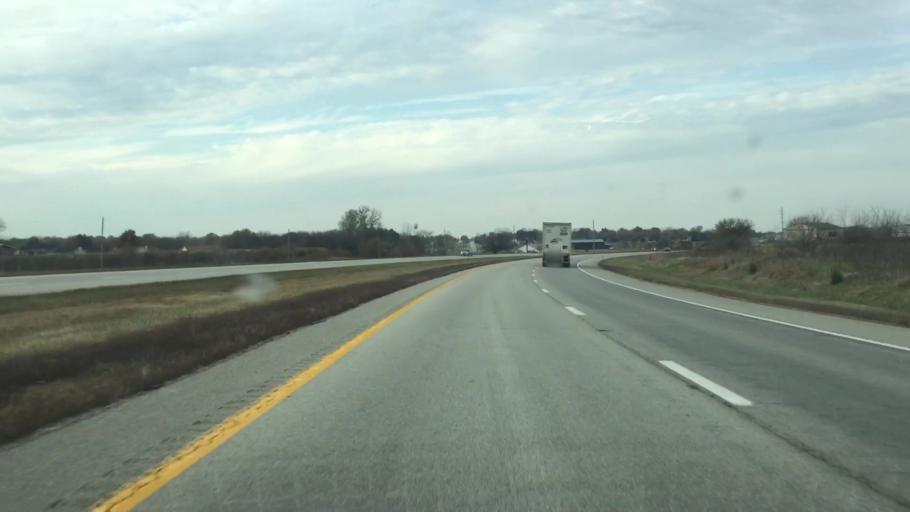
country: US
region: Missouri
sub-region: Cass County
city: Garden City
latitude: 38.5522
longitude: -94.1765
